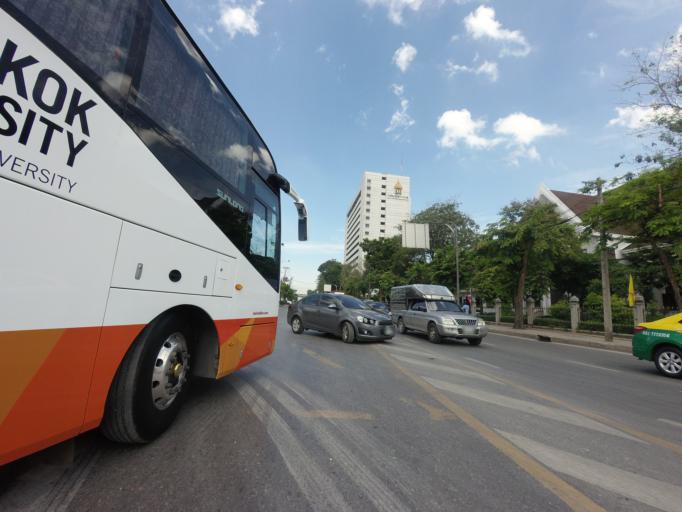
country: TH
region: Bangkok
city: Khlong Toei
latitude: 13.7142
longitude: 100.5662
